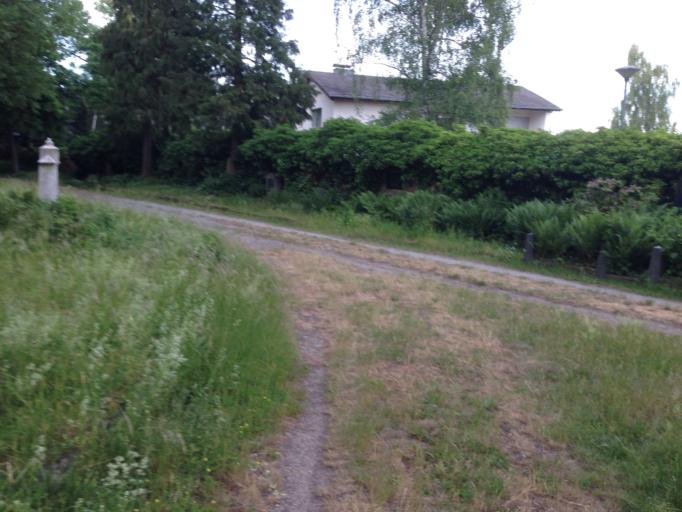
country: DE
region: Hesse
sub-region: Regierungsbezirk Giessen
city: Giessen
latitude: 50.5806
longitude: 8.6889
